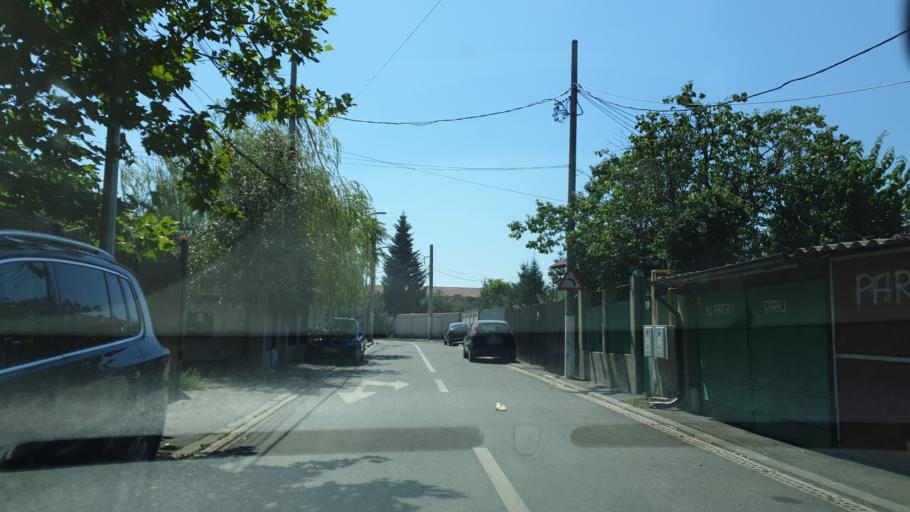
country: RO
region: Ilfov
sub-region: Comuna Chiajna
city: Rosu
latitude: 44.4672
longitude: 26.0221
